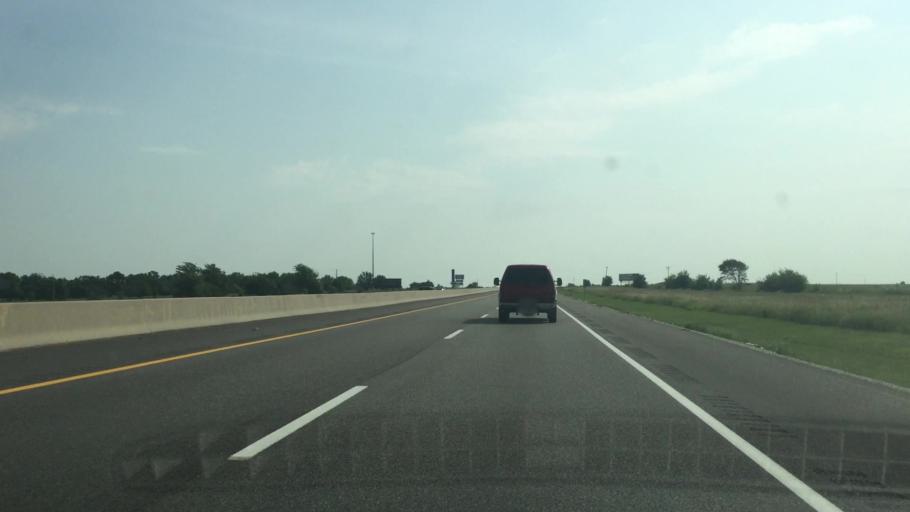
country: US
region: Kansas
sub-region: Butler County
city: Towanda
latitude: 37.7744
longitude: -96.9659
